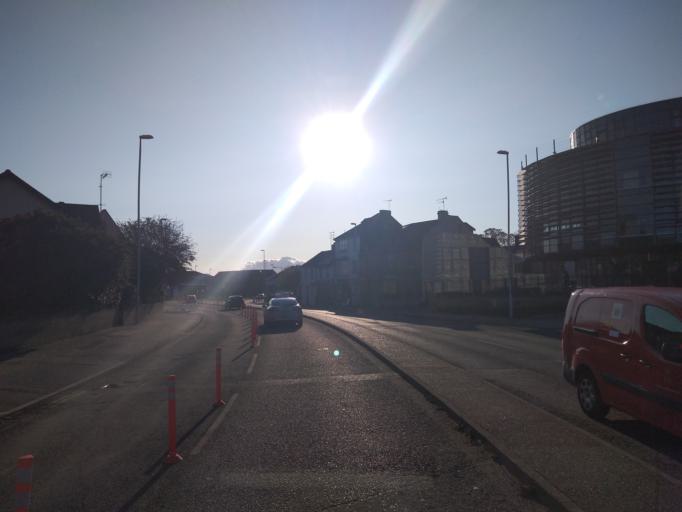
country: GB
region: England
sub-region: West Sussex
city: Worthing
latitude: 50.8155
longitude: -0.3709
